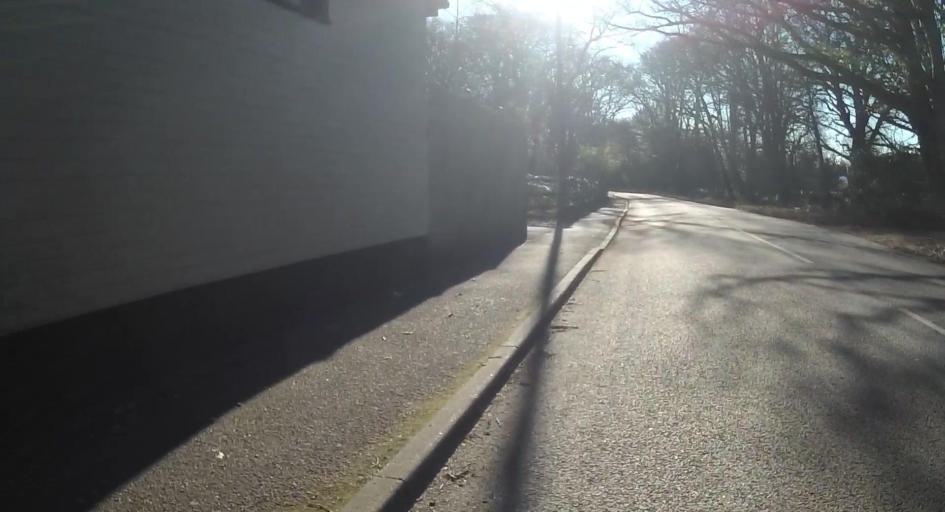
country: GB
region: England
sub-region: Surrey
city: Chobham
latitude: 51.3404
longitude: -0.6086
